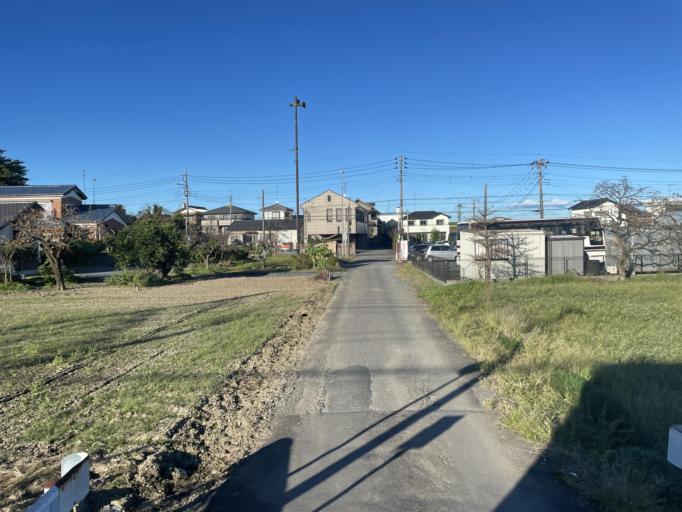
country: JP
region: Ibaraki
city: Koga
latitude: 36.2015
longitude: 139.6700
